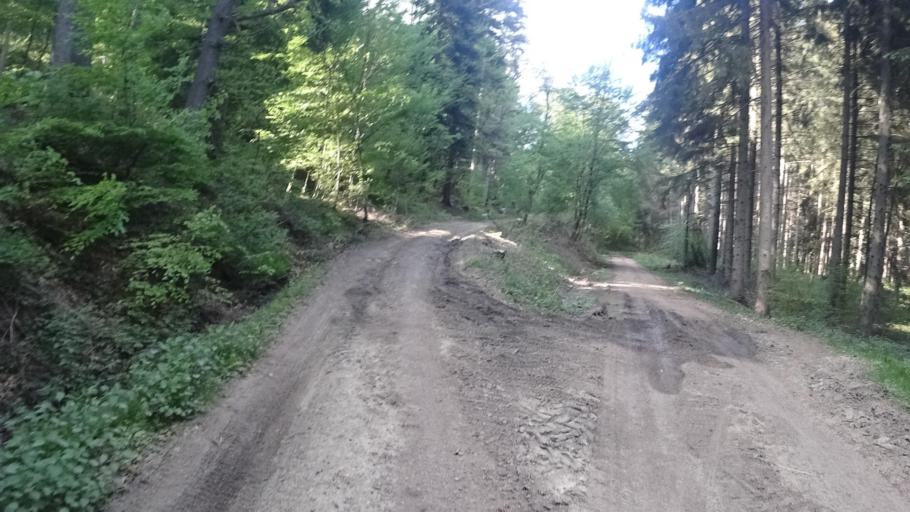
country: DE
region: Rheinland-Pfalz
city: Kirchsahr
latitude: 50.4940
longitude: 6.8973
